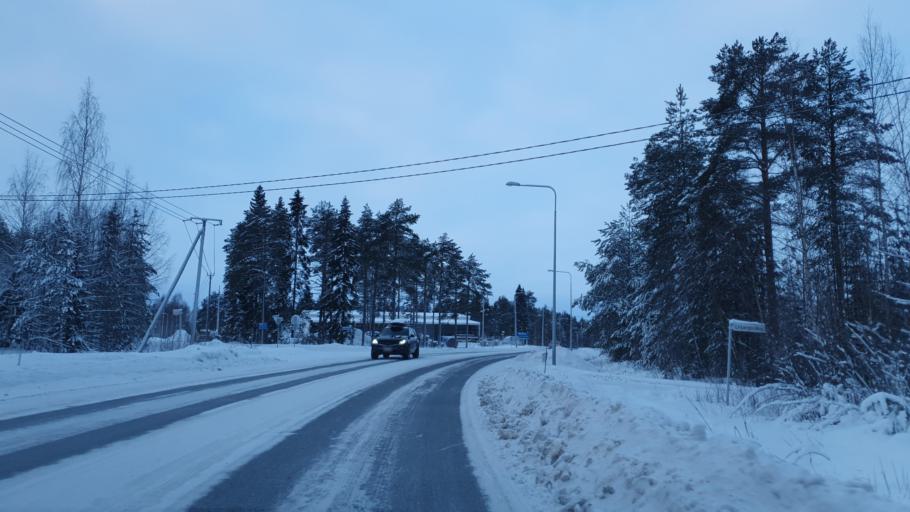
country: FI
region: Northern Ostrobothnia
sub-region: Oulu
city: Haukipudas
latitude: 65.1923
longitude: 25.3626
